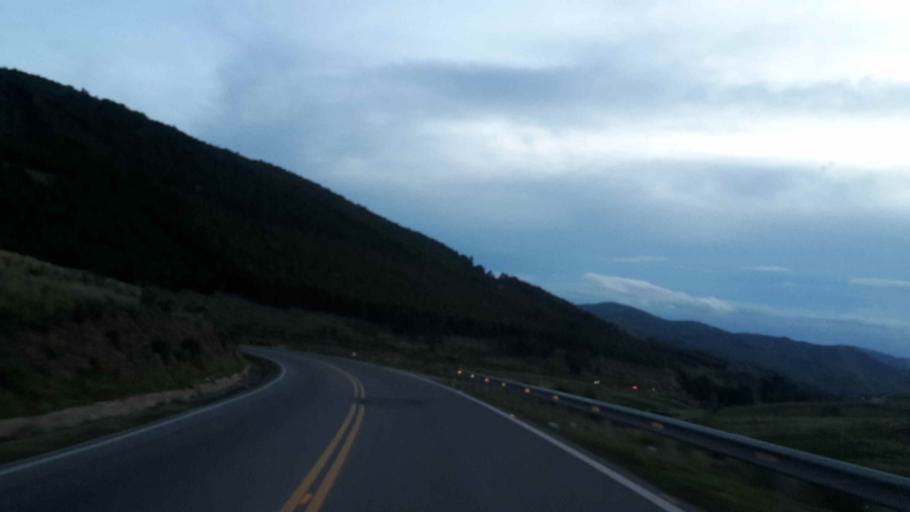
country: BO
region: Cochabamba
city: Colomi
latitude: -17.4030
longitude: -65.8791
